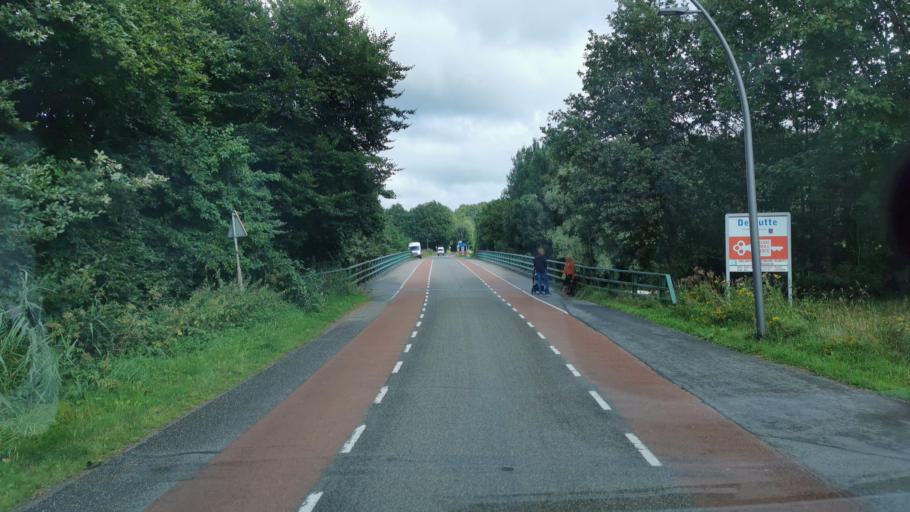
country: NL
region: Overijssel
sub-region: Gemeente Losser
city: Losser
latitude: 52.3075
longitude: 6.9912
